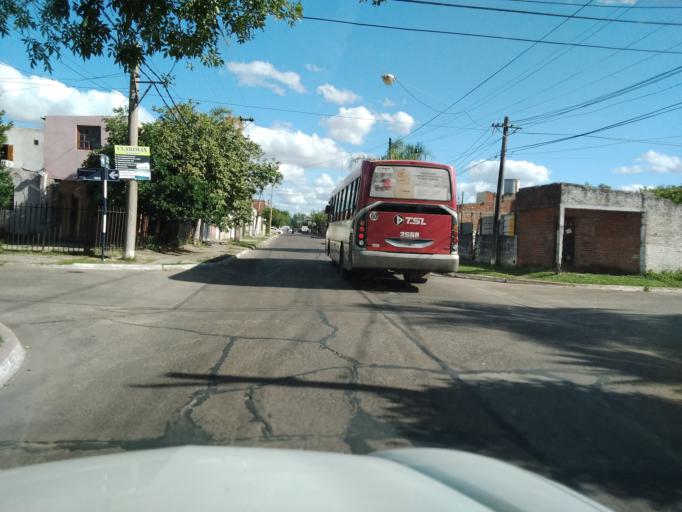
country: AR
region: Corrientes
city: Corrientes
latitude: -27.4919
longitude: -58.8333
